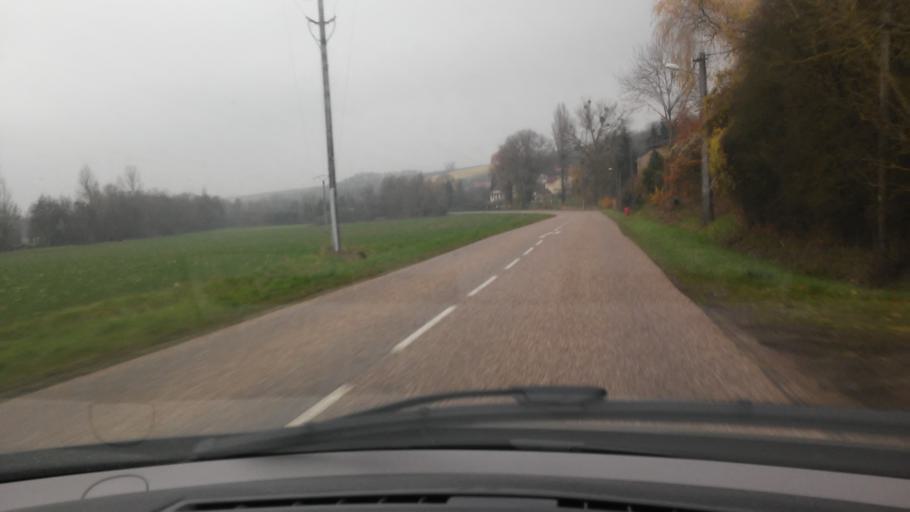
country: FR
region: Lorraine
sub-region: Departement de la Moselle
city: Courcelles-Chaussy
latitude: 49.1146
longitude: 6.4725
